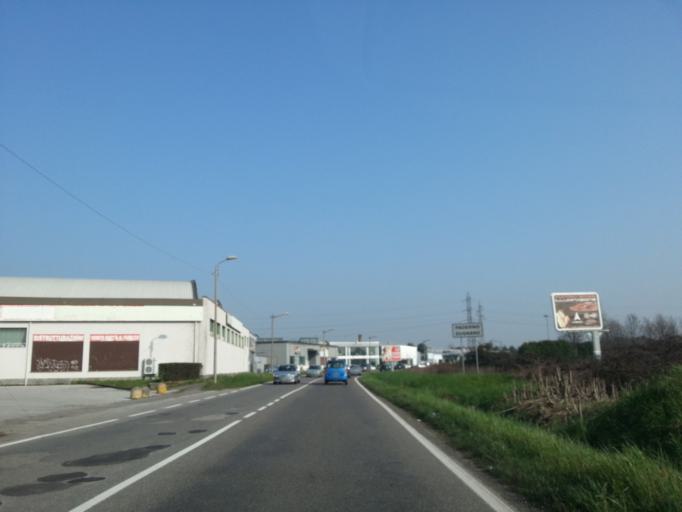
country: IT
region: Lombardy
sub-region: Citta metropolitana di Milano
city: Cusano Milanino
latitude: 45.5613
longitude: 9.1861
